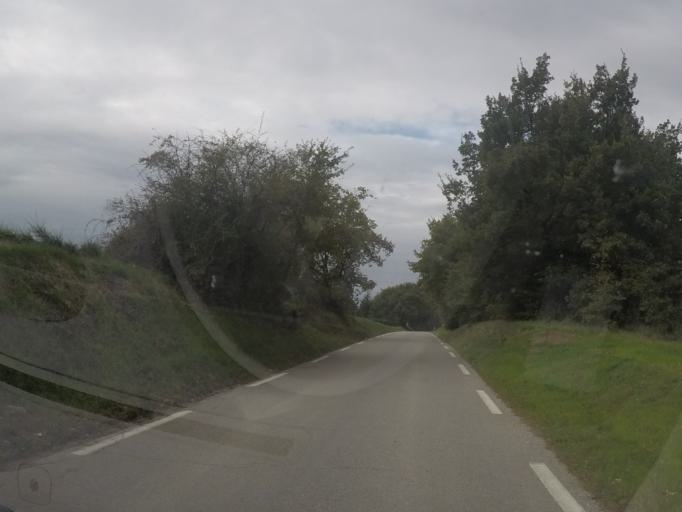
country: FR
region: Provence-Alpes-Cote d'Azur
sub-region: Departement du Vaucluse
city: Ansouis
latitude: 43.7416
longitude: 5.4571
